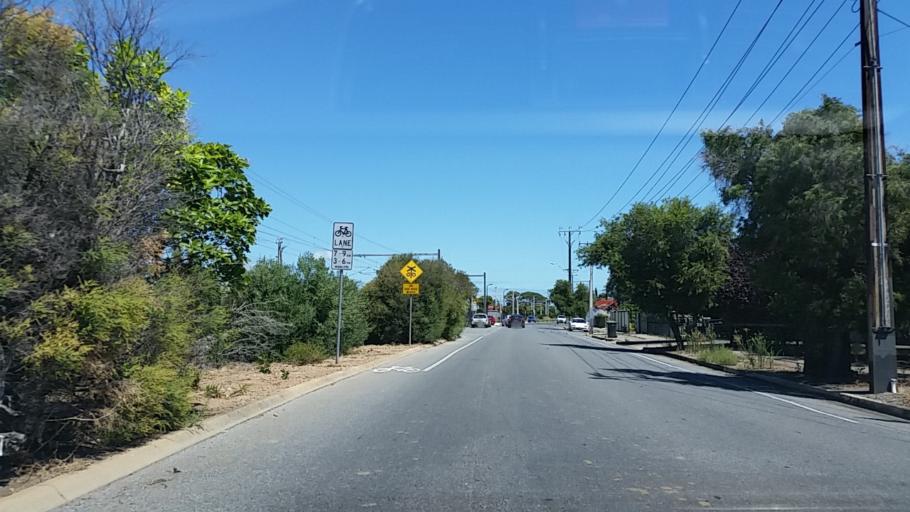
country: AU
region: South Australia
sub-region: Marion
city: South Plympton
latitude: -34.9859
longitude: 138.5653
